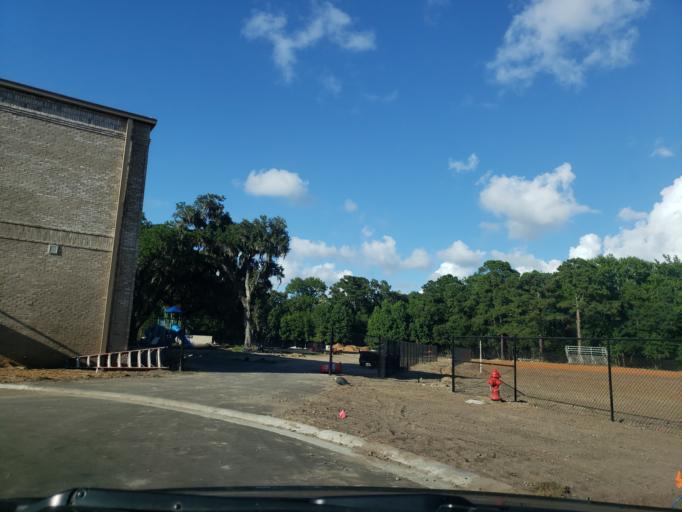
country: US
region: Georgia
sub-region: Chatham County
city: Montgomery
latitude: 31.9902
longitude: -81.1264
